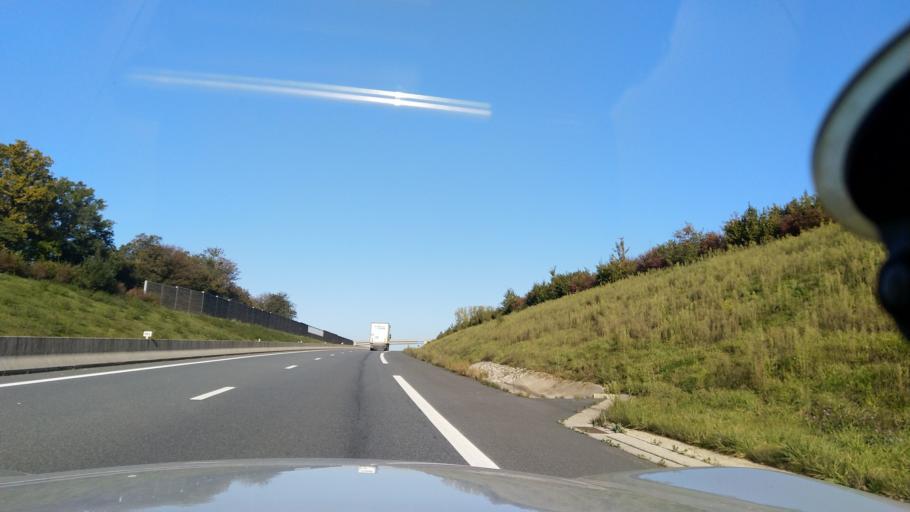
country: FR
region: Haute-Normandie
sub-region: Departement de la Seine-Maritime
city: Villers-Ecalles
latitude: 49.5380
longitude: 0.9341
